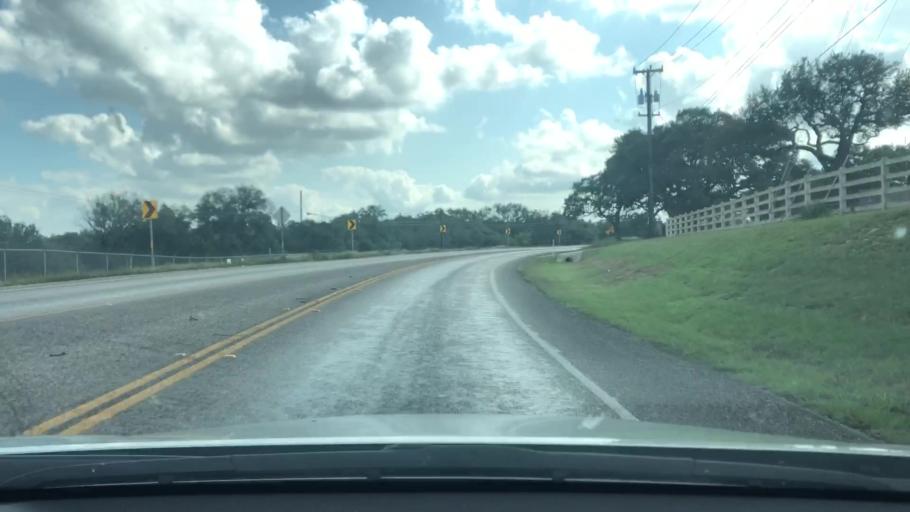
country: US
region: Texas
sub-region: Bexar County
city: Fair Oaks Ranch
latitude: 29.7186
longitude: -98.6237
